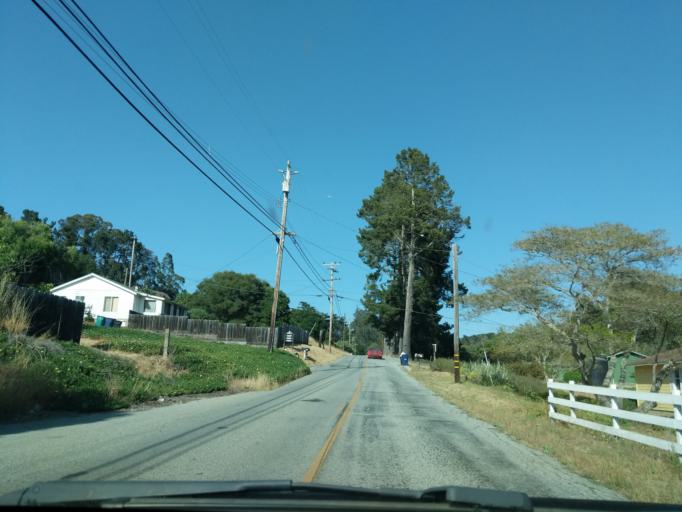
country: US
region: California
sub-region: Monterey County
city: Prunedale
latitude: 36.7970
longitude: -121.6521
